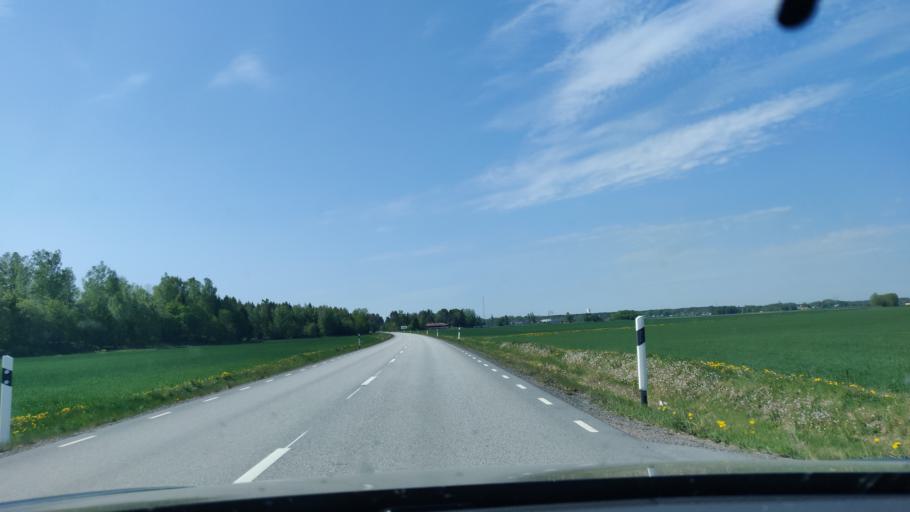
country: SE
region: Uppsala
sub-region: Heby Kommun
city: OEstervala
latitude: 60.1621
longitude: 17.2019
